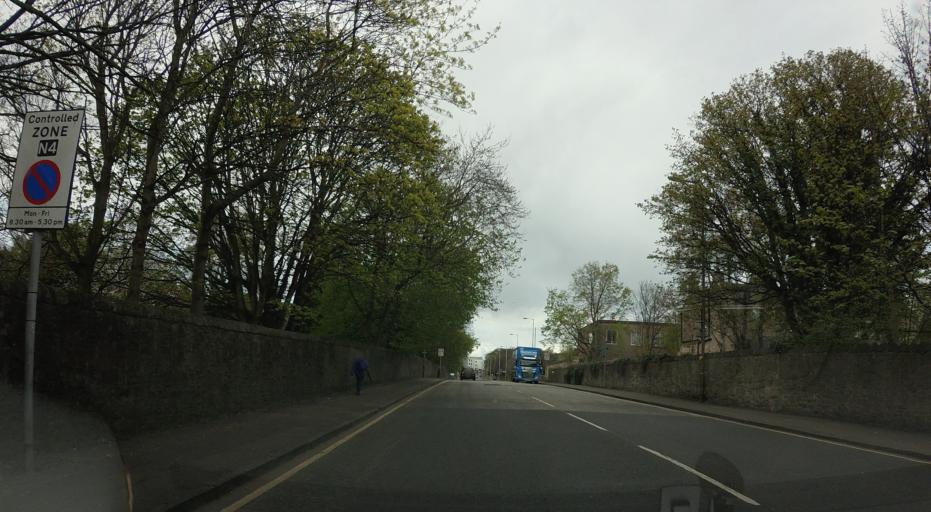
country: GB
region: Scotland
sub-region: Edinburgh
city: Edinburgh
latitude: 55.9588
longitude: -3.2267
